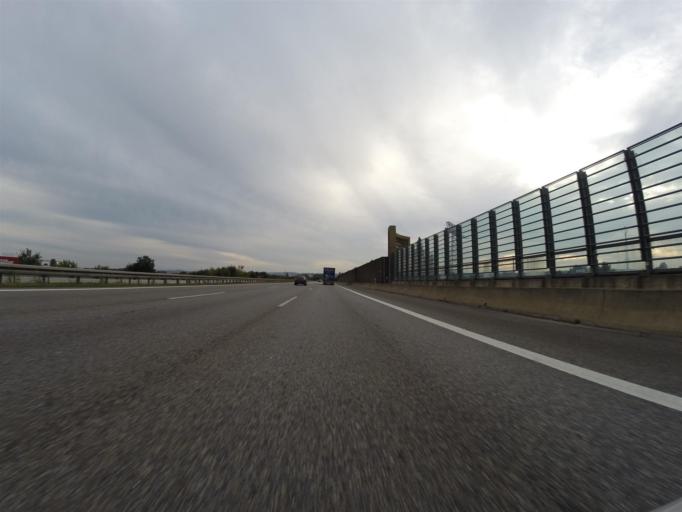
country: DE
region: Saxony
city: Radebeul
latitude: 51.0869
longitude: 13.6913
